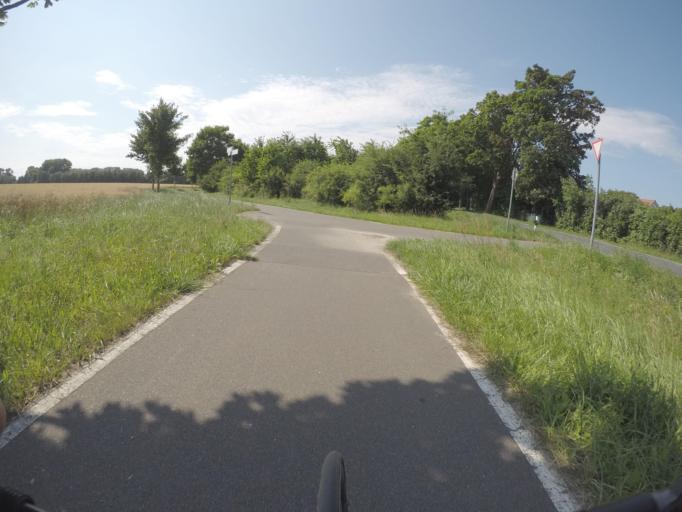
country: DE
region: Mecklenburg-Vorpommern
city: Gingst
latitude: 54.4459
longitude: 13.2030
